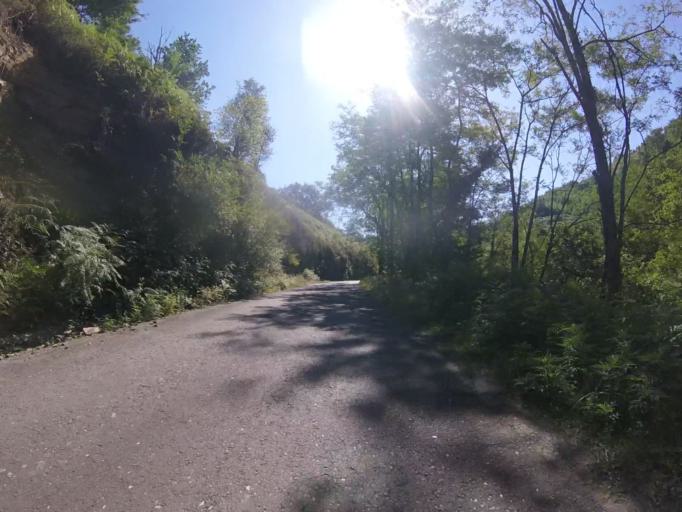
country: ES
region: Navarre
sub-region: Provincia de Navarra
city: Goizueta
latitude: 43.1896
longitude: -1.8492
